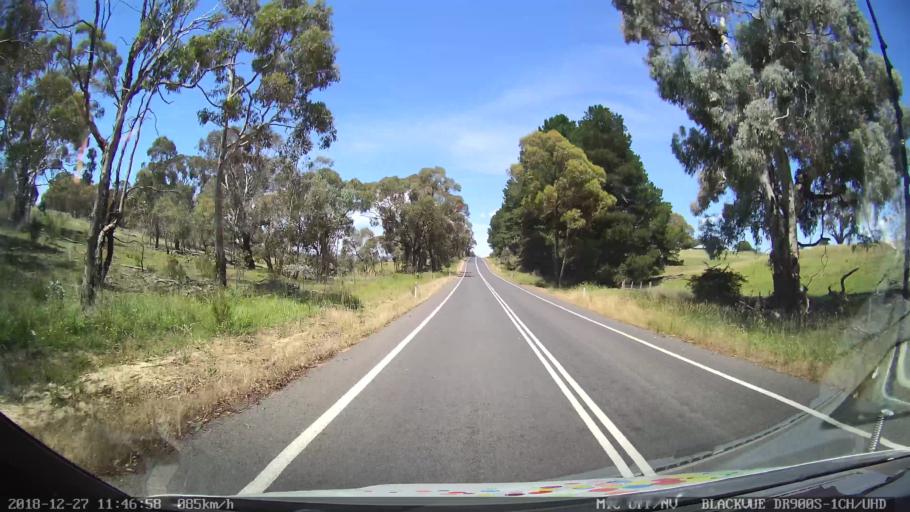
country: AU
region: New South Wales
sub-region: Bathurst Regional
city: Perthville
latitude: -33.5916
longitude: 149.4501
